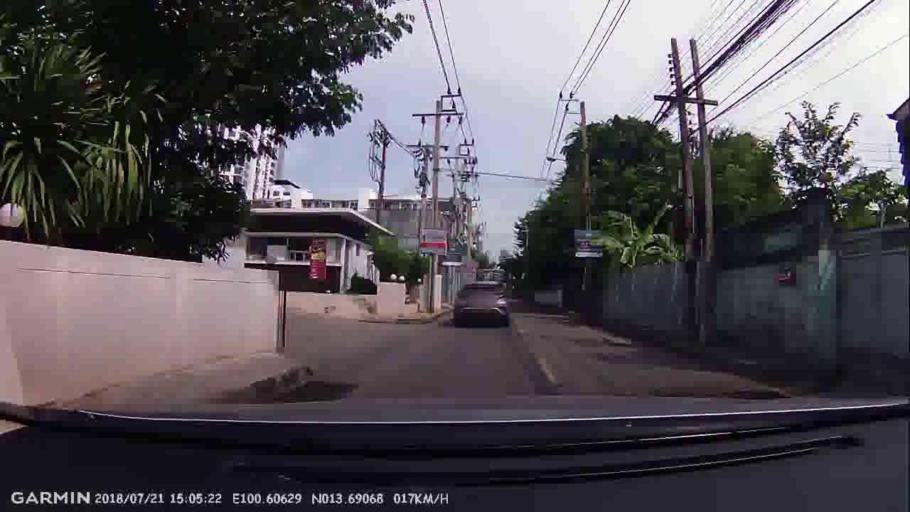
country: TH
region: Bangkok
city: Phra Khanong
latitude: 13.6906
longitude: 100.6063
